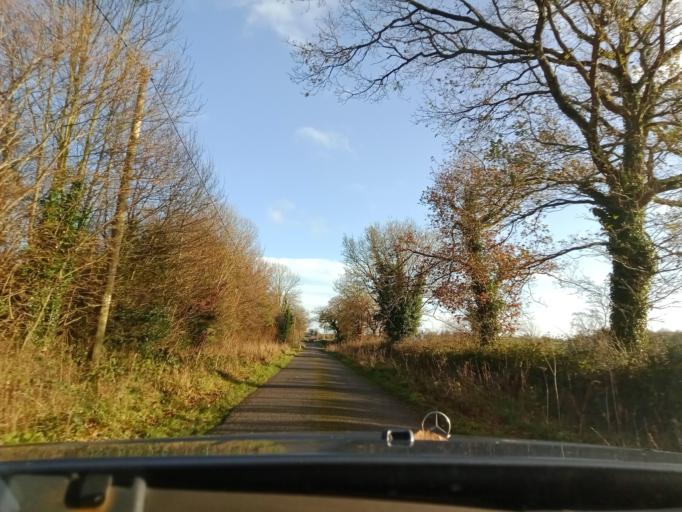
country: IE
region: Leinster
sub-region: Kilkenny
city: Callan
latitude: 52.5012
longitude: -7.4127
